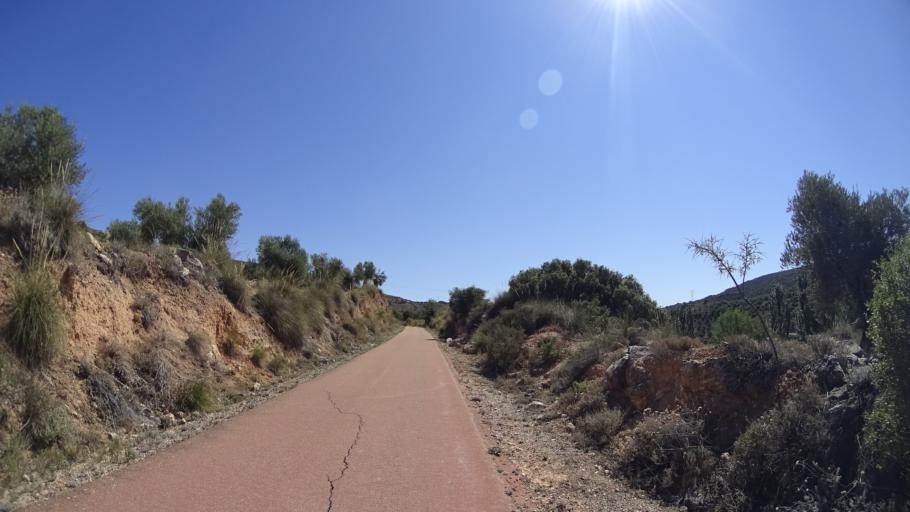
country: ES
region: Madrid
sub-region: Provincia de Madrid
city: Perales de Tajuna
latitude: 40.2312
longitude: -3.3722
